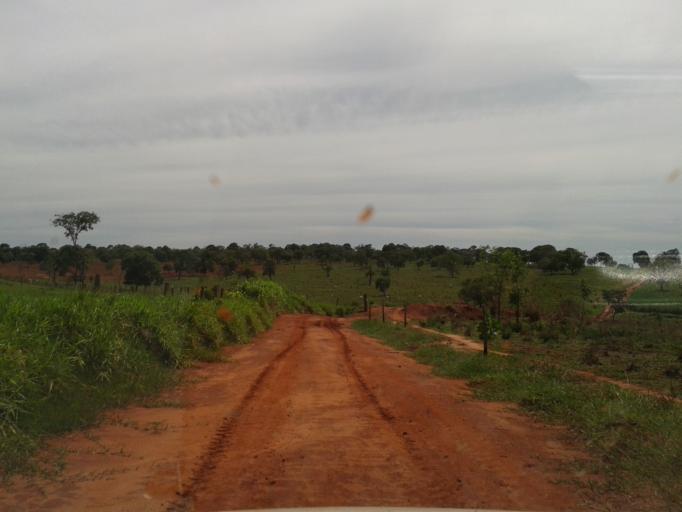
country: BR
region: Minas Gerais
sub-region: Santa Vitoria
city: Santa Vitoria
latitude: -19.2090
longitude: -50.6503
